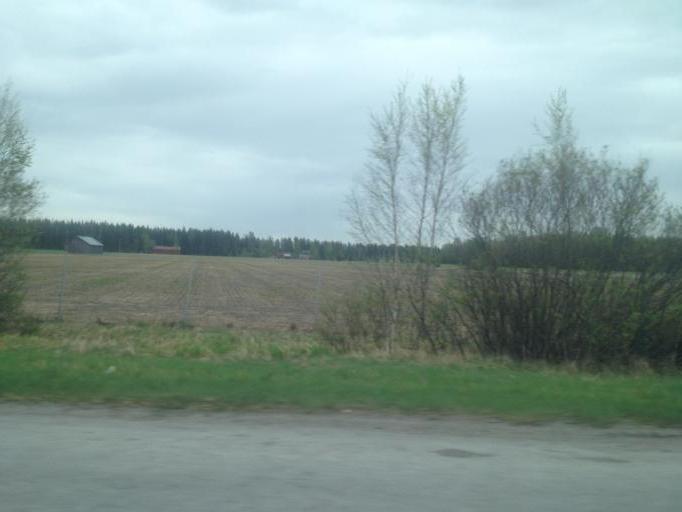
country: FI
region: Uusimaa
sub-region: Helsinki
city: Nurmijaervi
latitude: 60.5119
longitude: 24.8481
